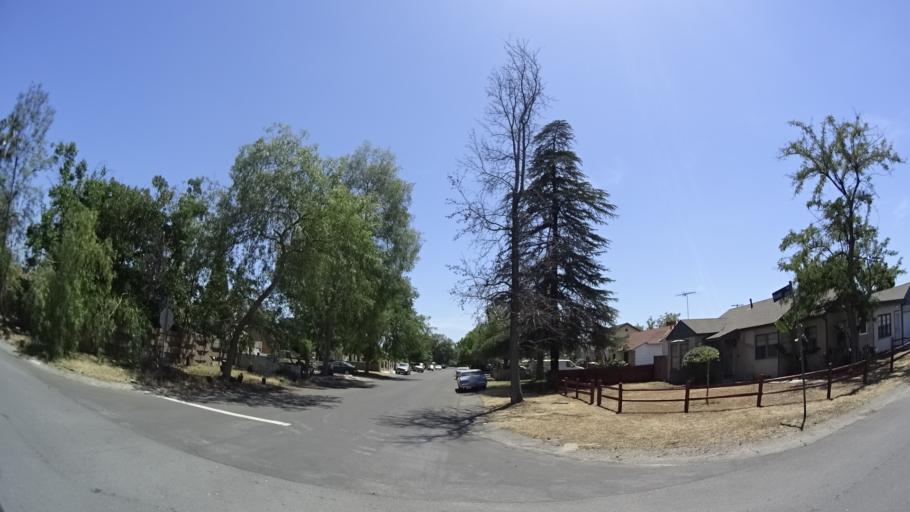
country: US
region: California
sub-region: Los Angeles County
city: North Hollywood
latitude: 34.1849
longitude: -118.3758
